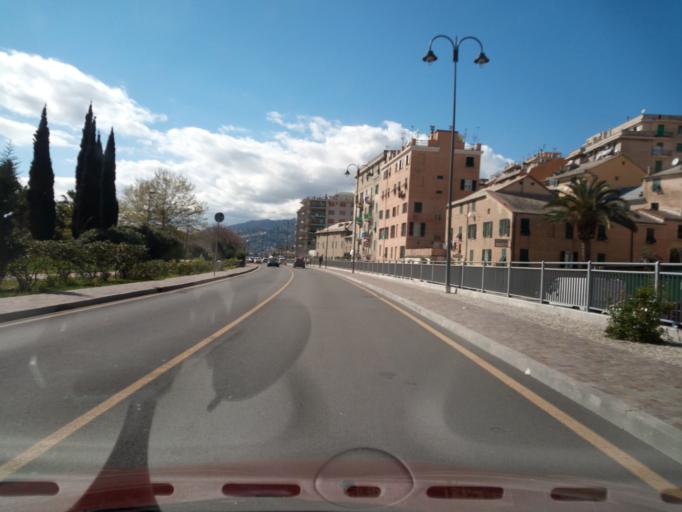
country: IT
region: Liguria
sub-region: Provincia di Genova
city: Mele
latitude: 44.4274
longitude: 8.7812
